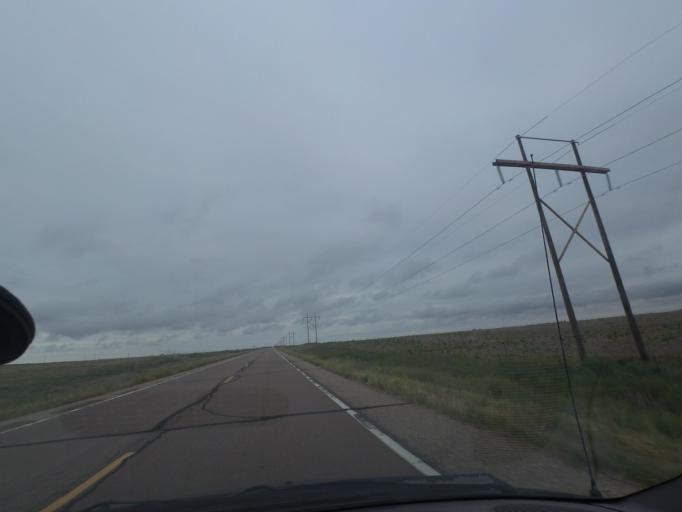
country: US
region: Colorado
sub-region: Yuma County
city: Yuma
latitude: 39.6558
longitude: -102.7316
